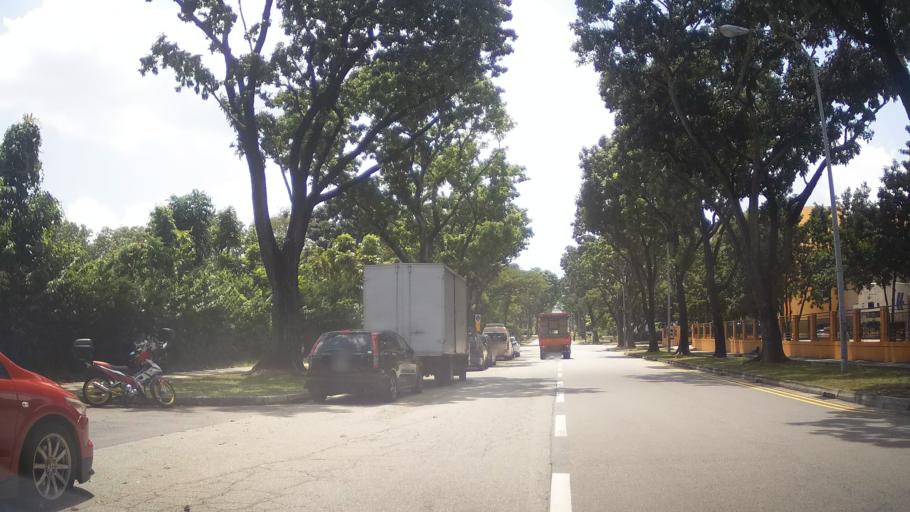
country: MY
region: Johor
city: Johor Bahru
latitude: 1.3299
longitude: 103.7102
